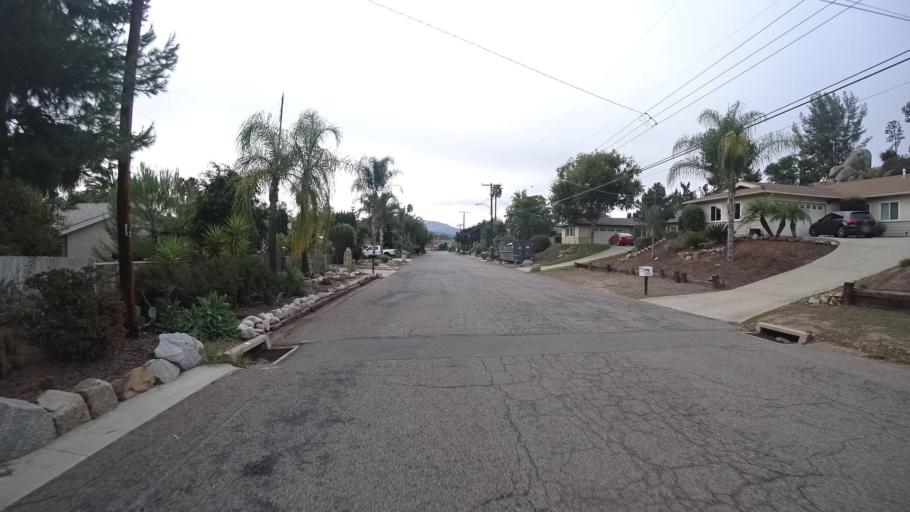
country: US
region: California
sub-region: San Diego County
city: Rancho San Diego
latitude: 32.7608
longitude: -116.9261
